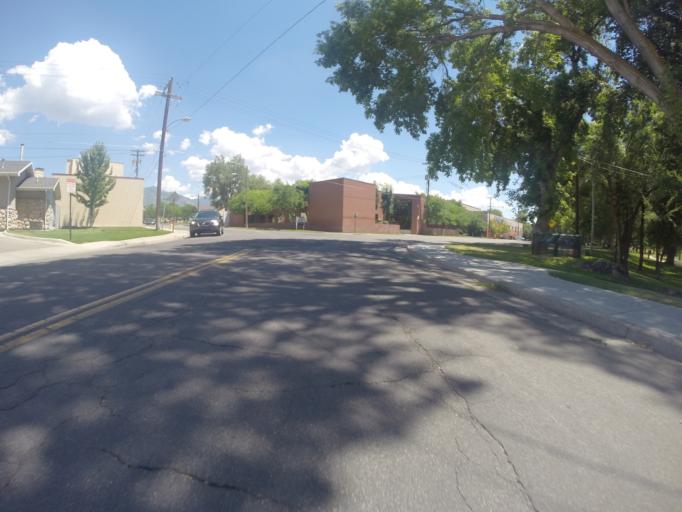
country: US
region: Utah
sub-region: Salt Lake County
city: Willard
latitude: 40.7221
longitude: -111.8599
